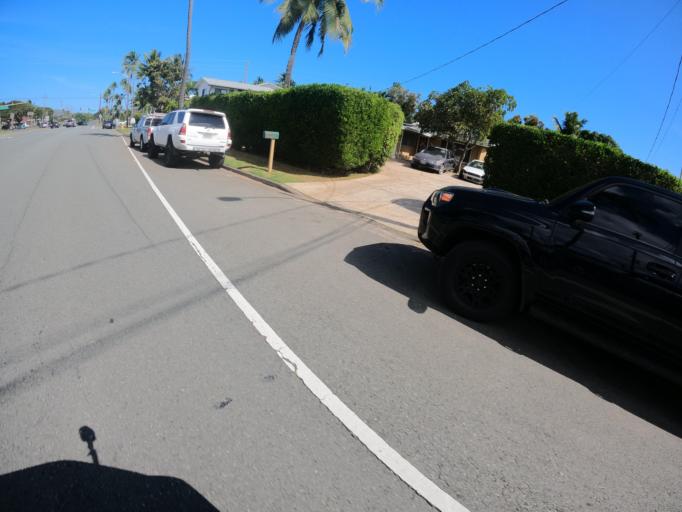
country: US
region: Hawaii
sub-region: Honolulu County
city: Kailua
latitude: 21.4203
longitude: -157.7488
